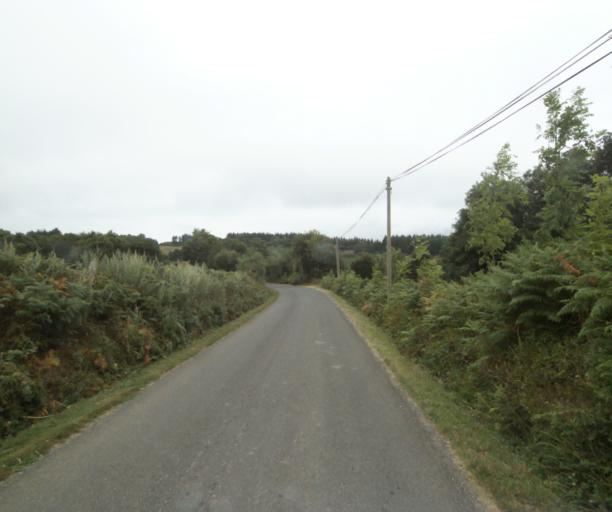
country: FR
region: Midi-Pyrenees
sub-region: Departement du Tarn
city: Soreze
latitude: 43.4089
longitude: 2.0559
